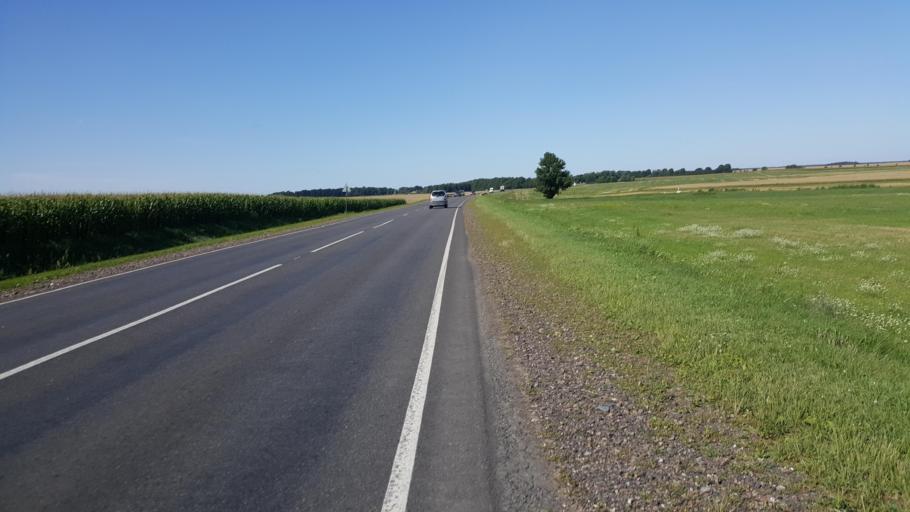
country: BY
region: Brest
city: Charnawchytsy
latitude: 52.2499
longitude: 23.7516
